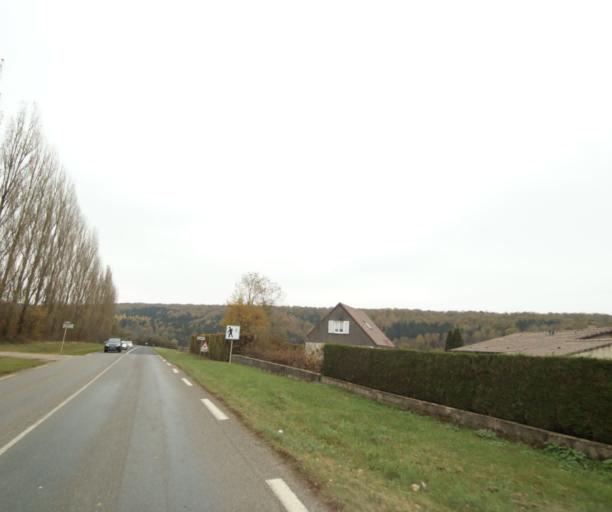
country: FR
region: Lorraine
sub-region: Departement de Meurthe-et-Moselle
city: Briey
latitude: 49.2698
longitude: 5.9223
